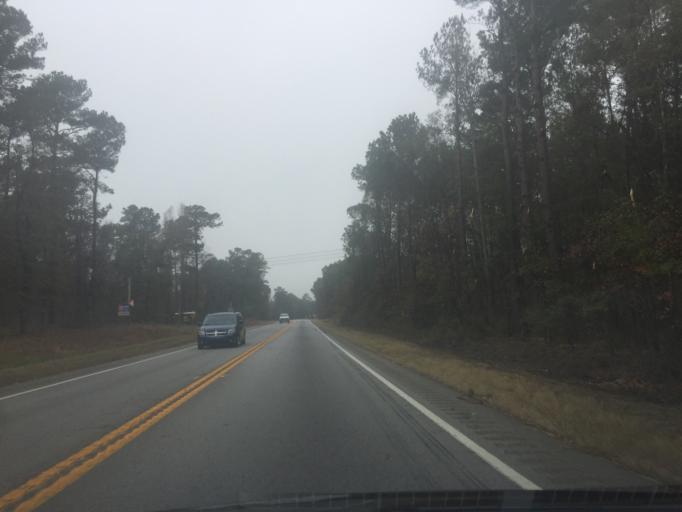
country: US
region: Georgia
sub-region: Chatham County
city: Georgetown
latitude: 32.0077
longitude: -81.2896
